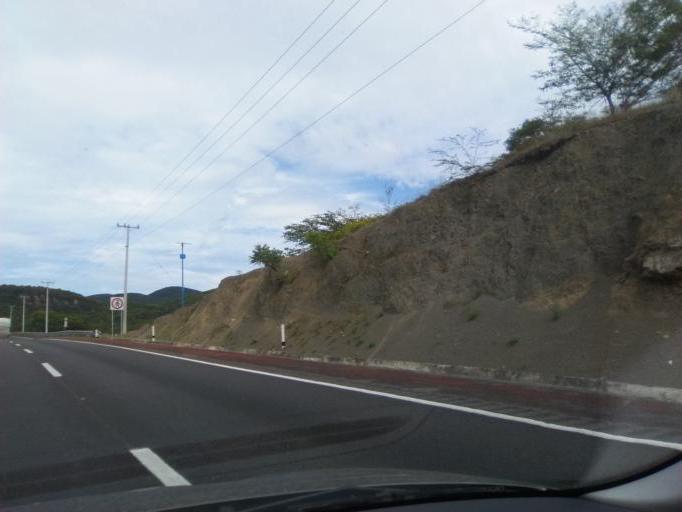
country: MX
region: Guerrero
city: Zumpango del Rio
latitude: 17.6573
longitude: -99.4986
